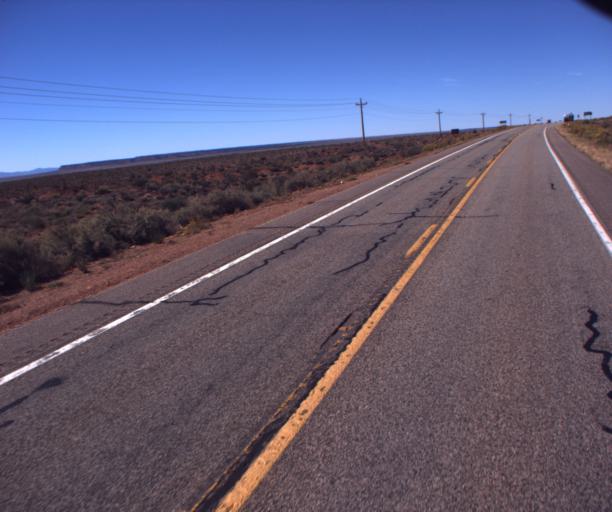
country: US
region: Arizona
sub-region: Coconino County
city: Fredonia
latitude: 36.8577
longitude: -112.7318
